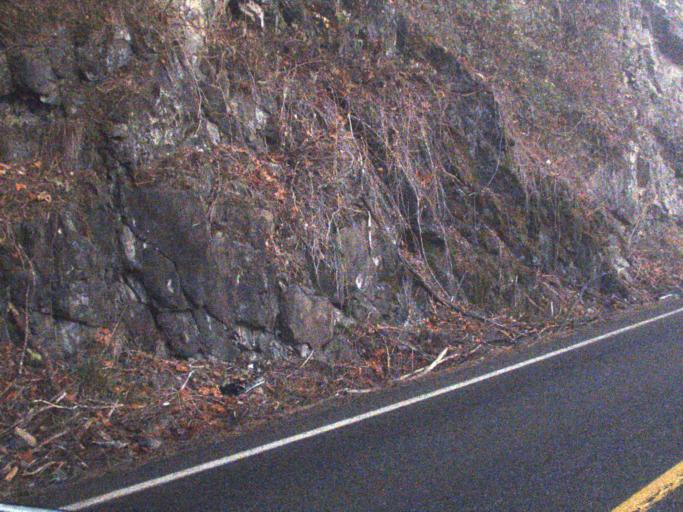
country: US
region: Washington
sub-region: Snohomish County
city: Darrington
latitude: 48.4920
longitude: -121.5653
